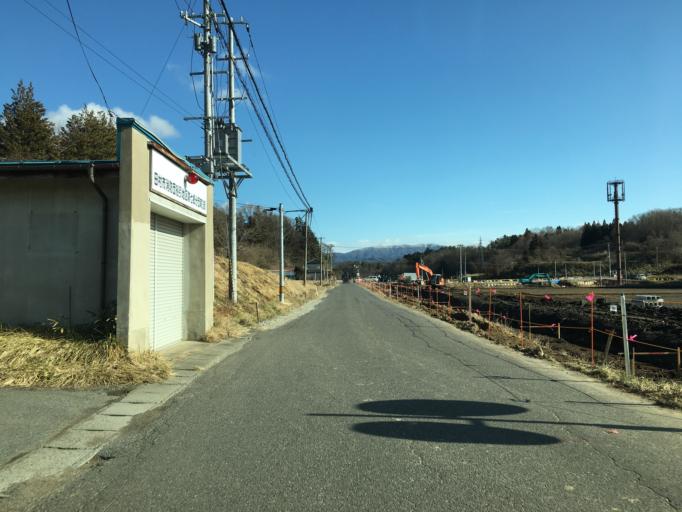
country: JP
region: Fukushima
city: Funehikimachi-funehiki
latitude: 37.4147
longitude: 140.5770
